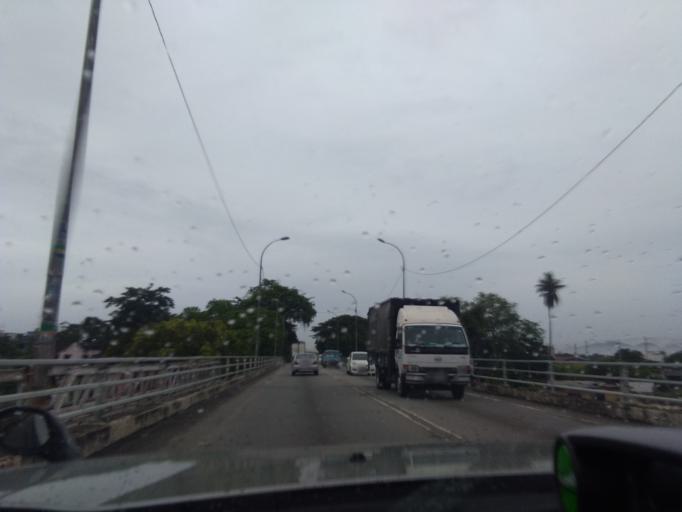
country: MY
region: Penang
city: Nibong Tebal
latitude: 5.1640
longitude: 100.4789
